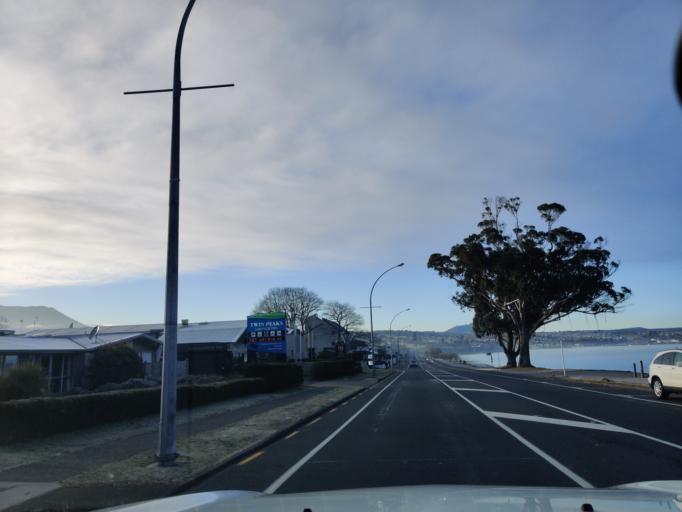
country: NZ
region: Waikato
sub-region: Taupo District
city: Taupo
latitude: -38.6937
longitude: 176.0765
